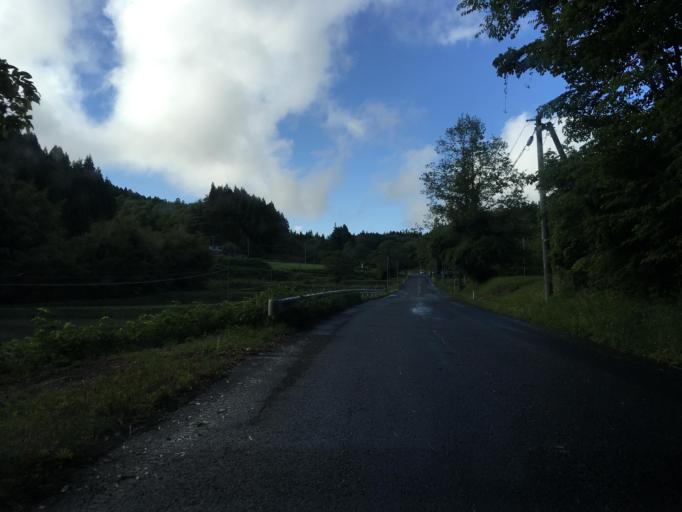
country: JP
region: Iwate
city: Ichinoseki
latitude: 38.8755
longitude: 141.4261
